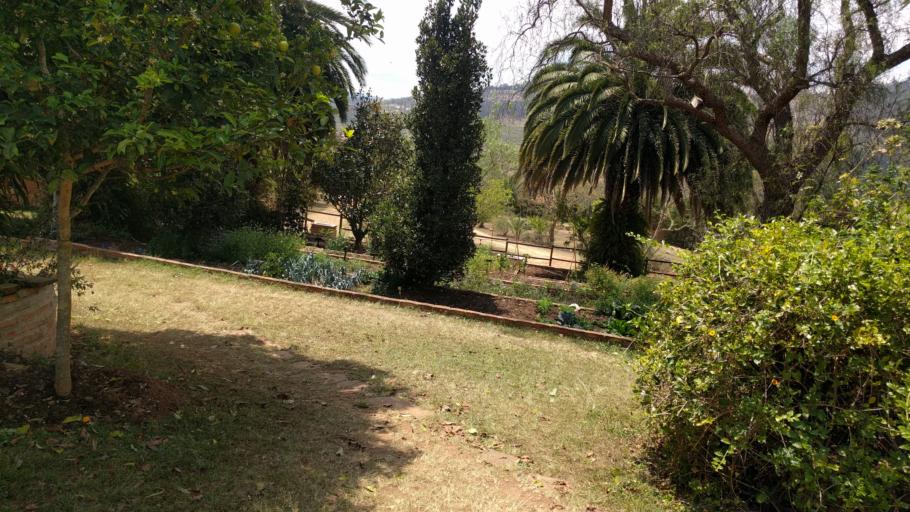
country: BO
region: Santa Cruz
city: Samaipata
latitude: -18.1884
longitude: -63.8803
